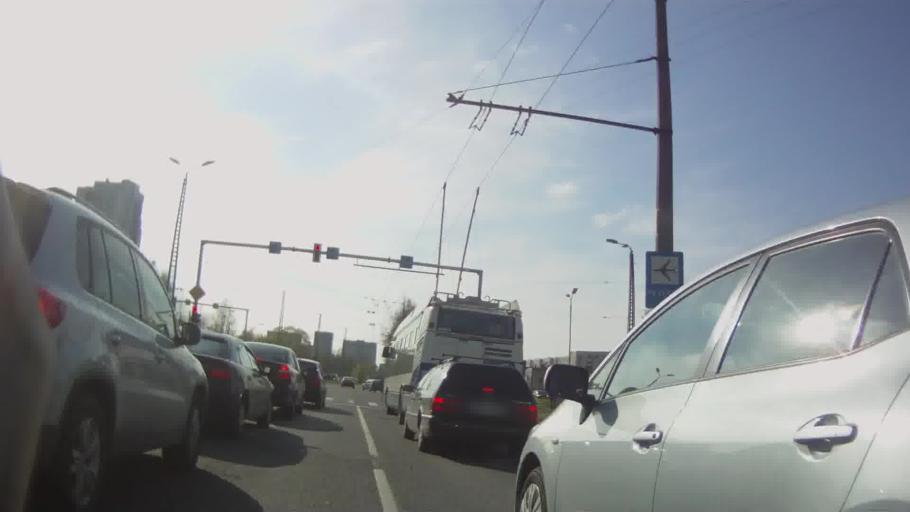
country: LV
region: Riga
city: Jaunciems
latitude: 56.9567
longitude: 24.1905
